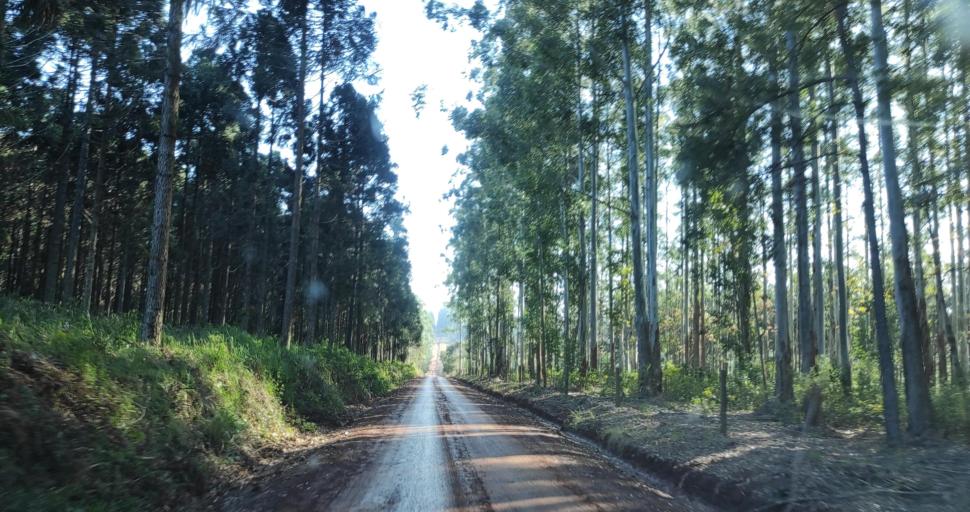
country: AR
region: Misiones
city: Capiovi
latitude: -26.8739
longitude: -55.0160
